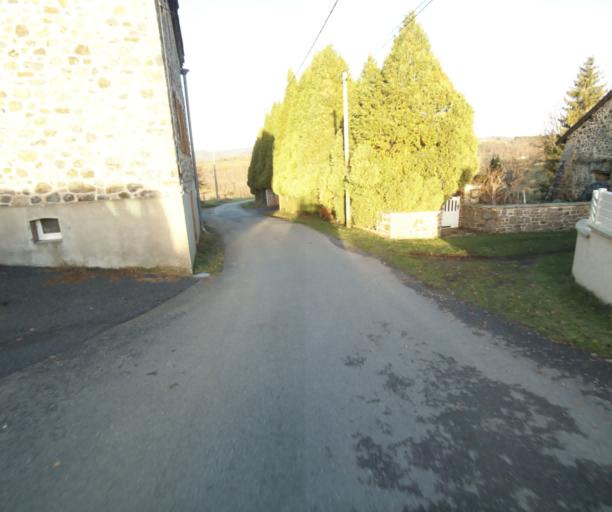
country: FR
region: Limousin
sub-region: Departement de la Correze
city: Laguenne
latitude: 45.2370
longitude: 1.8173
